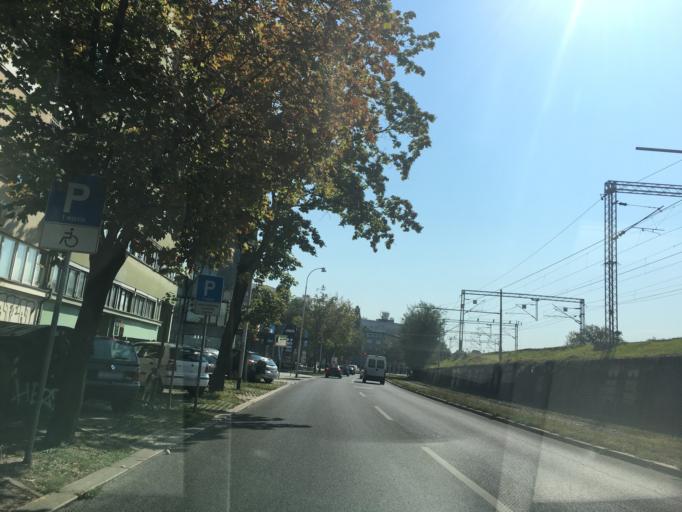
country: HR
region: Grad Zagreb
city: Zagreb - Centar
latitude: 45.8088
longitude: 15.9594
